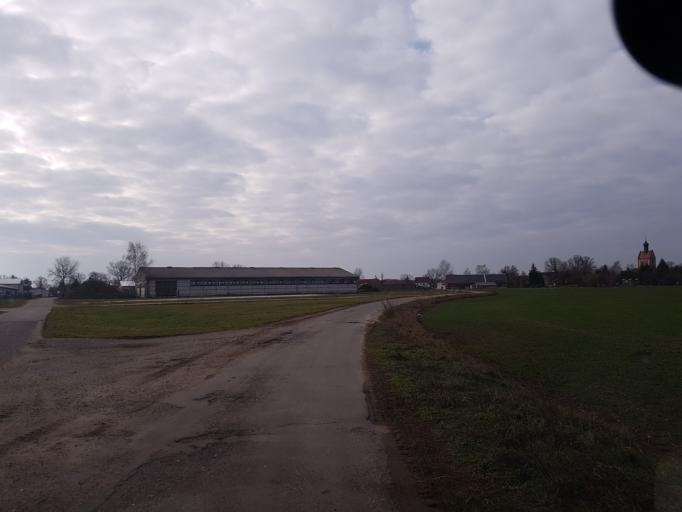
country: DE
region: Brandenburg
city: Doberlug-Kirchhain
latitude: 51.6565
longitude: 13.5405
